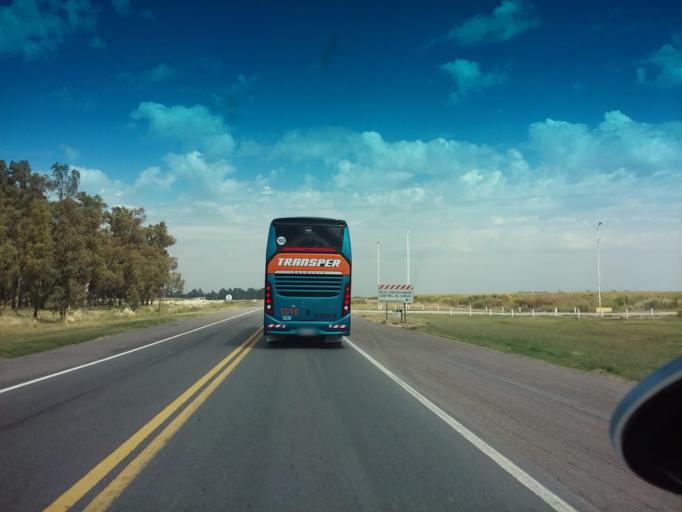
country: AR
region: Buenos Aires
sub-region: Partido de Carlos Casares
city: Carlos Casares
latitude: -35.6583
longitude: -61.4016
